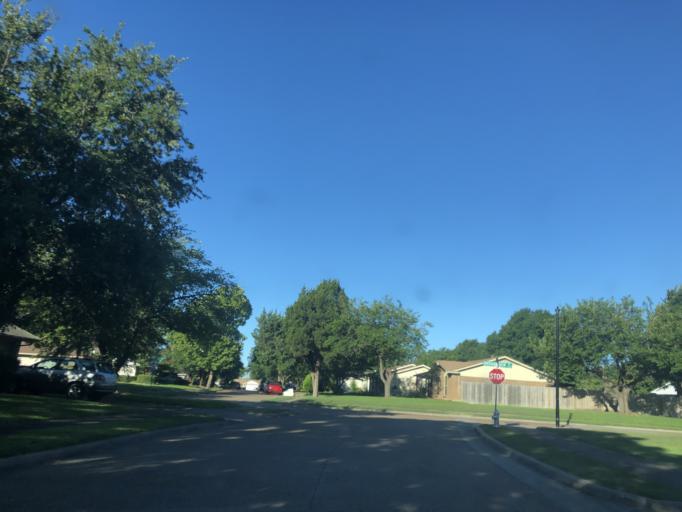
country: US
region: Texas
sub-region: Dallas County
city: Garland
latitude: 32.8527
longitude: -96.6379
